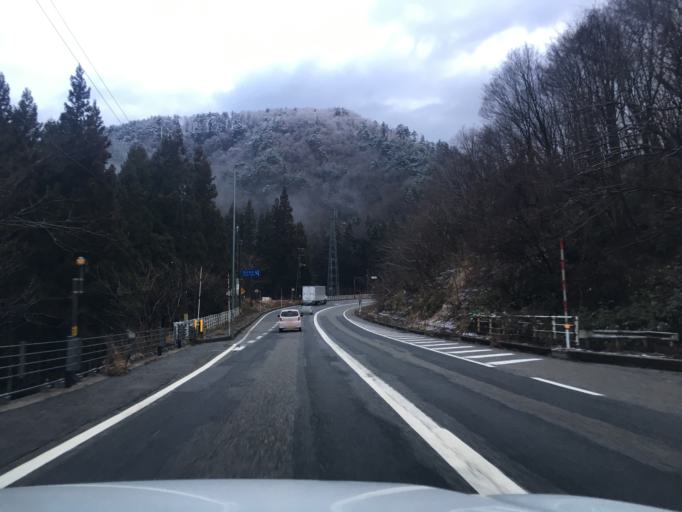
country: JP
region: Niigata
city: Murakami
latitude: 38.4210
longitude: 139.5675
